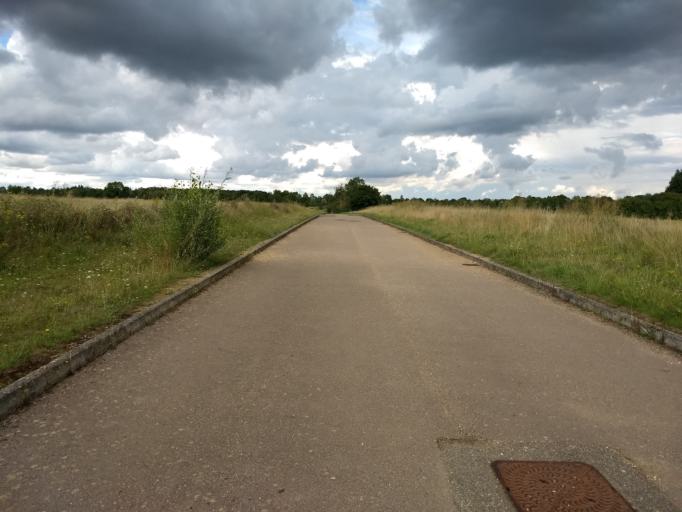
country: GB
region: England
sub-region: Buckinghamshire
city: Newton Longville
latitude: 51.9904
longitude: -0.7975
